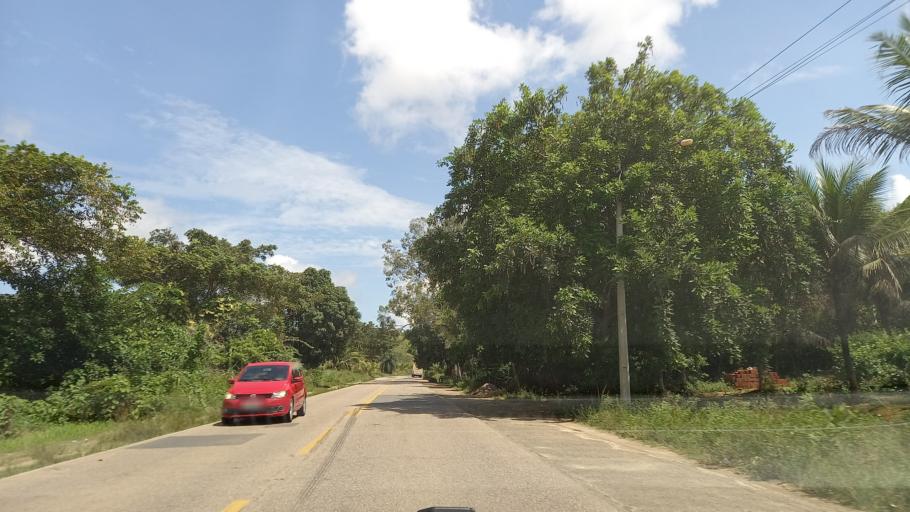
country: BR
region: Pernambuco
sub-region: Barreiros
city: Barreiros
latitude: -8.7786
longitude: -35.1744
